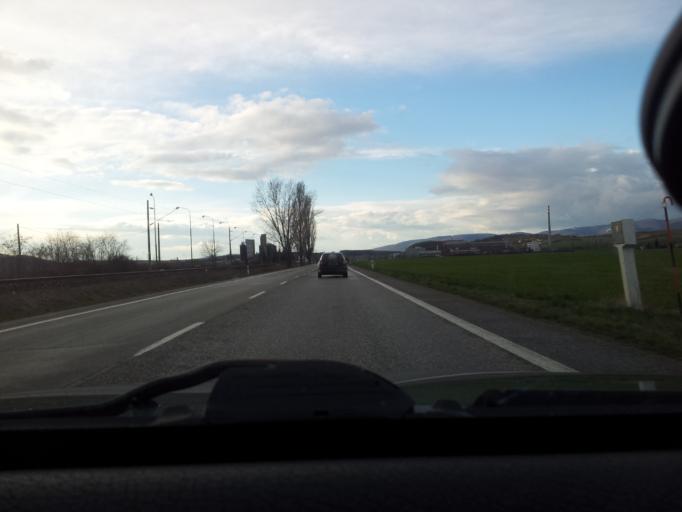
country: SK
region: Nitriansky
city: Tlmace
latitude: 48.2749
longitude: 18.5555
